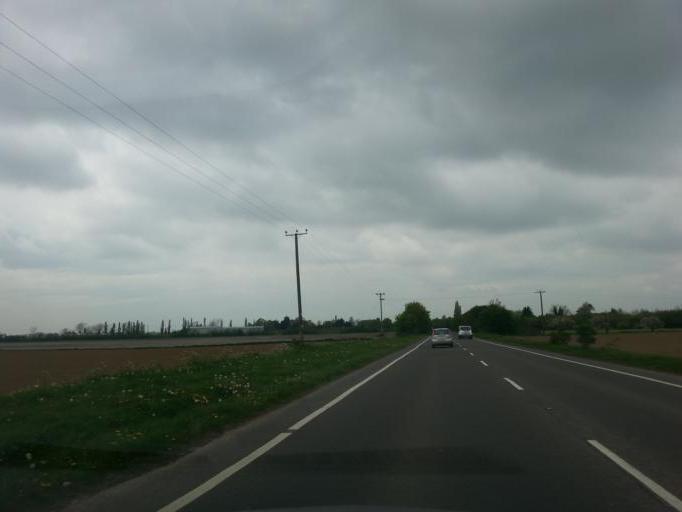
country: GB
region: England
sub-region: Norfolk
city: Emneth
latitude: 52.6277
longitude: 0.2083
